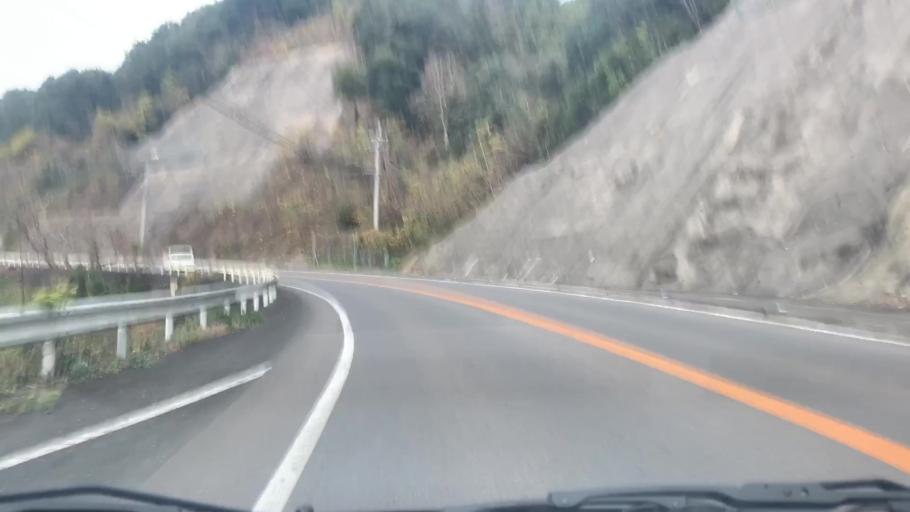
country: JP
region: Saga Prefecture
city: Ureshinomachi-shimojuku
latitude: 33.1367
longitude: 130.0244
